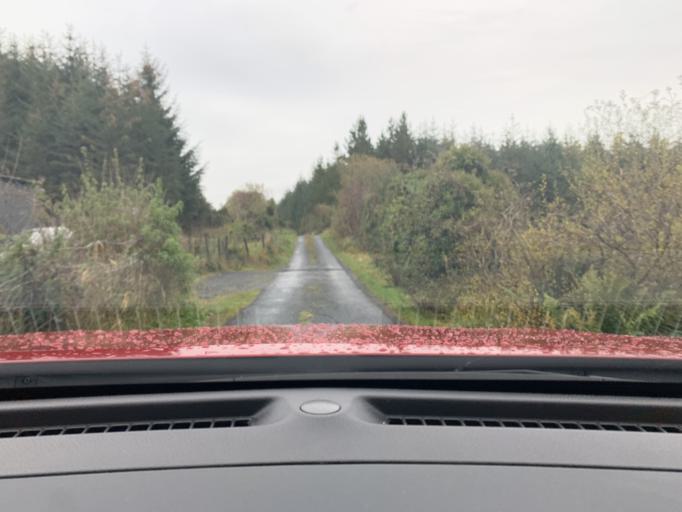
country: IE
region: Connaught
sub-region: Roscommon
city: Ballaghaderreen
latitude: 53.9239
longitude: -8.5662
